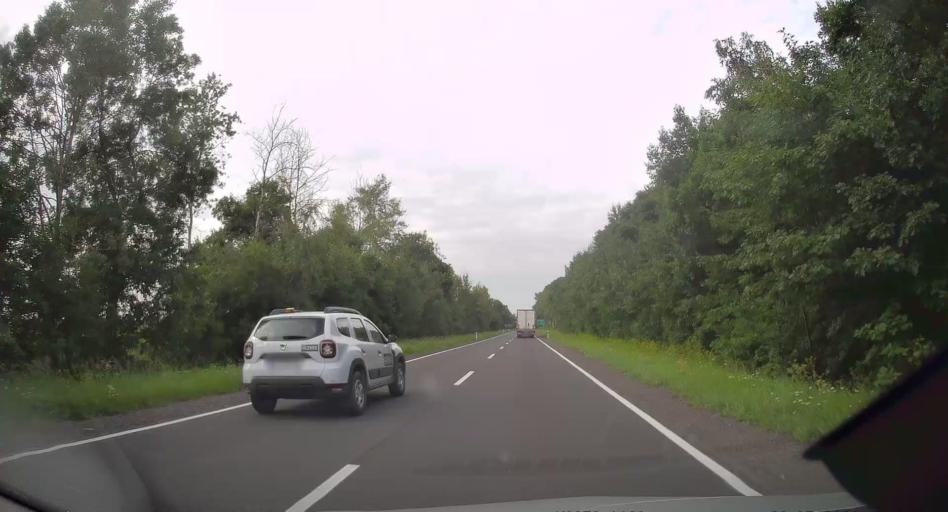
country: PL
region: Lodz Voivodeship
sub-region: Powiat radomszczanski
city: Plawno
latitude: 50.9591
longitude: 19.4040
